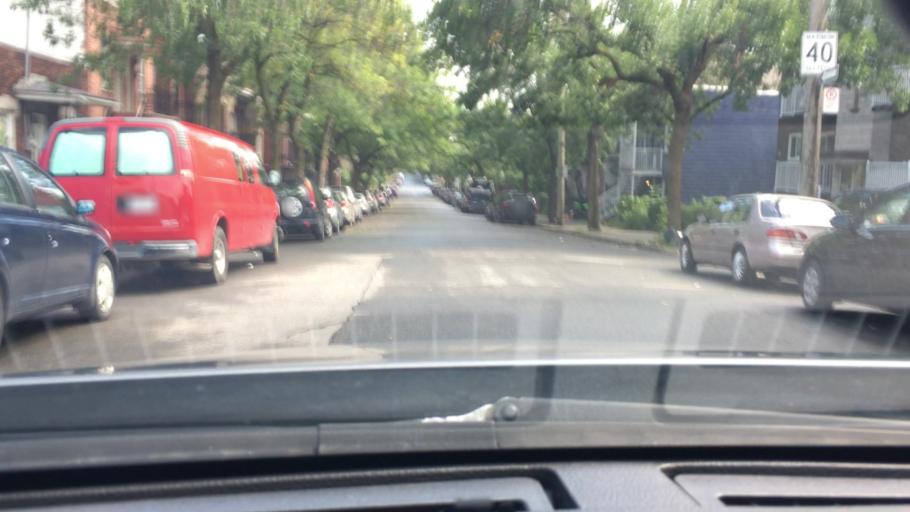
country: CA
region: Quebec
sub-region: Monteregie
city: Longueuil
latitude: 45.5386
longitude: -73.5562
